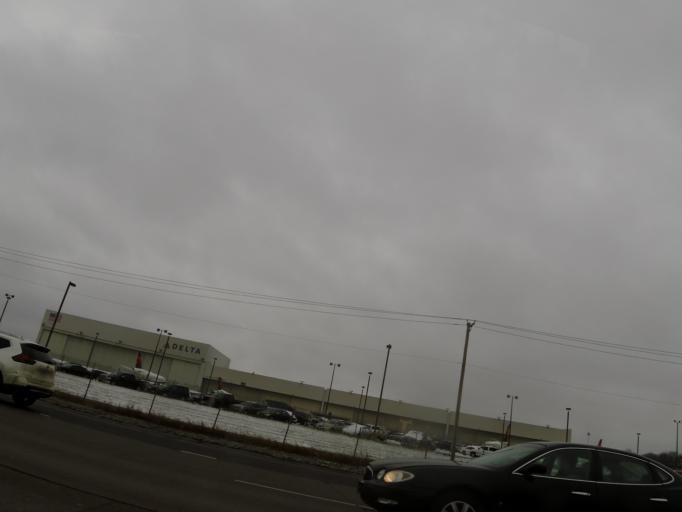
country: US
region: Minnesota
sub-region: Hennepin County
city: Richfield
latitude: 44.8623
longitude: -93.2285
